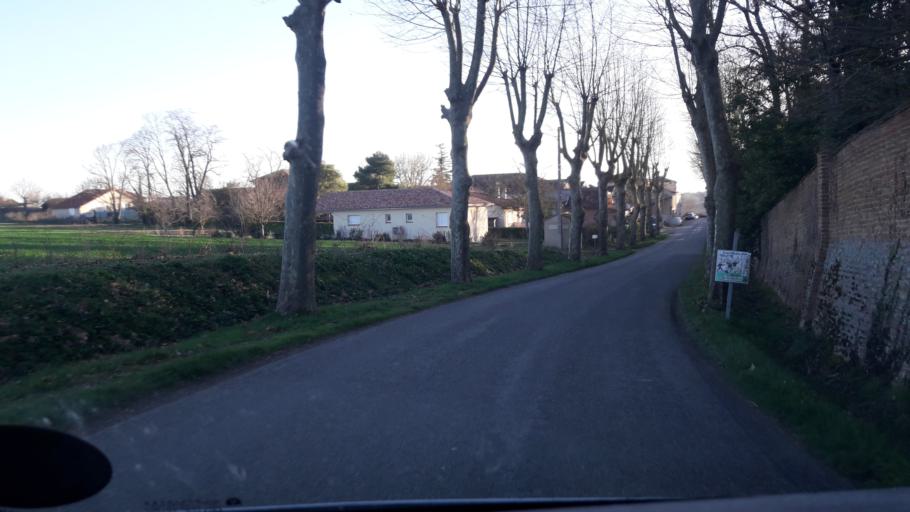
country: FR
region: Midi-Pyrenees
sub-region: Departement du Gers
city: Gimont
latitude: 43.5996
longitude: 0.9821
